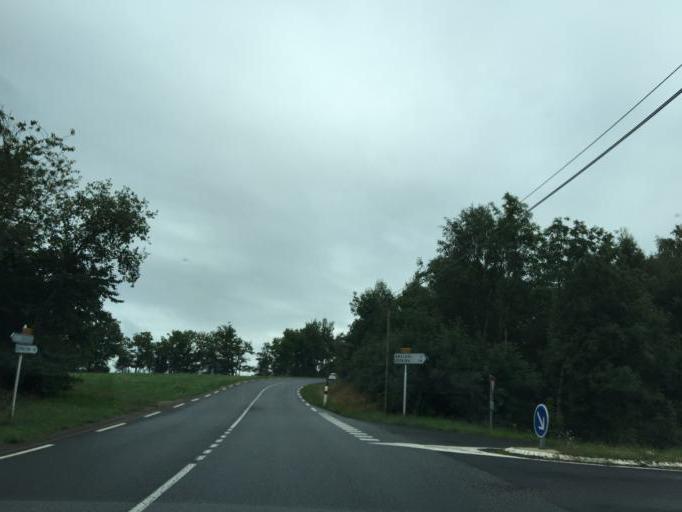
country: FR
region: Midi-Pyrenees
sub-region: Departement de l'Aveyron
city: Espalion
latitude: 44.6046
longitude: 2.7965
